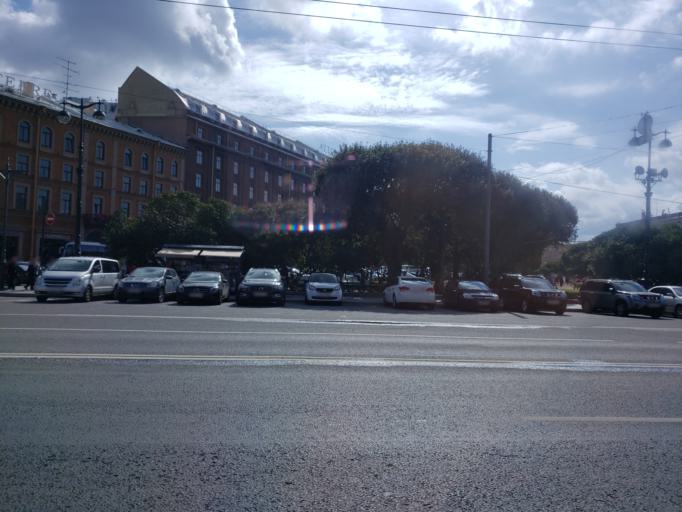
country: RU
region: St.-Petersburg
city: Saint Petersburg
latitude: 59.9338
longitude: 30.3076
